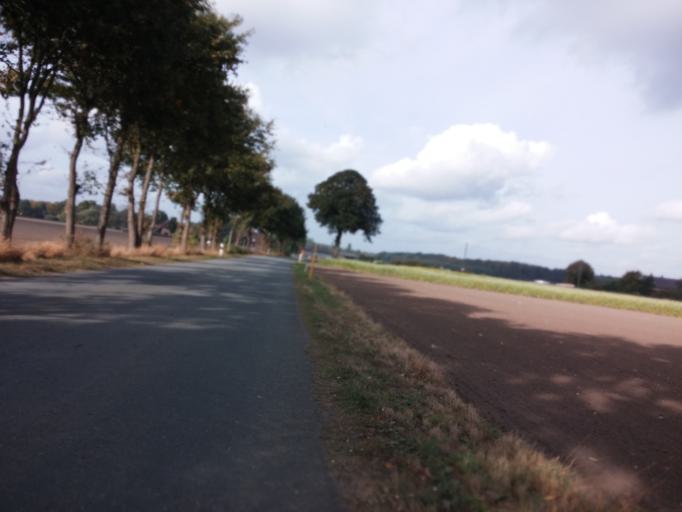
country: DE
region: North Rhine-Westphalia
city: Dorsten
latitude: 51.6409
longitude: 7.0138
